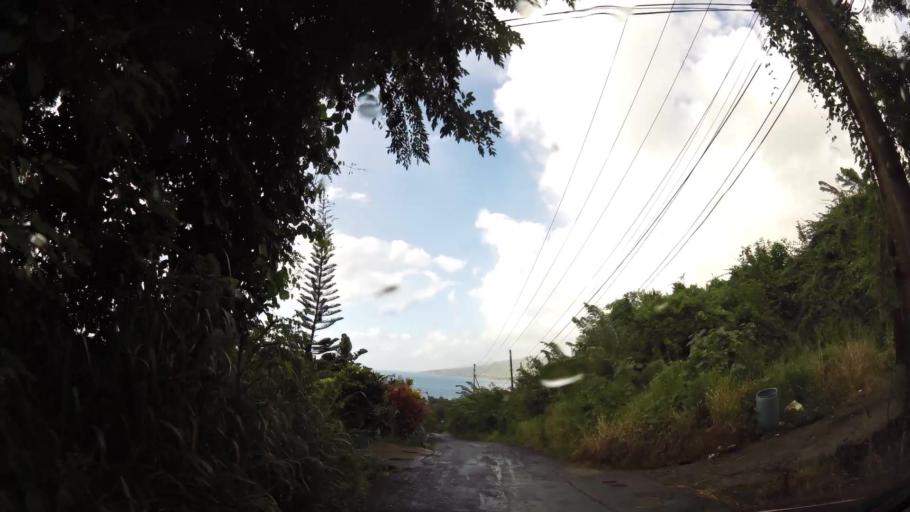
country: DM
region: Saint George
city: Roseau
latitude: 15.3249
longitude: -61.3907
